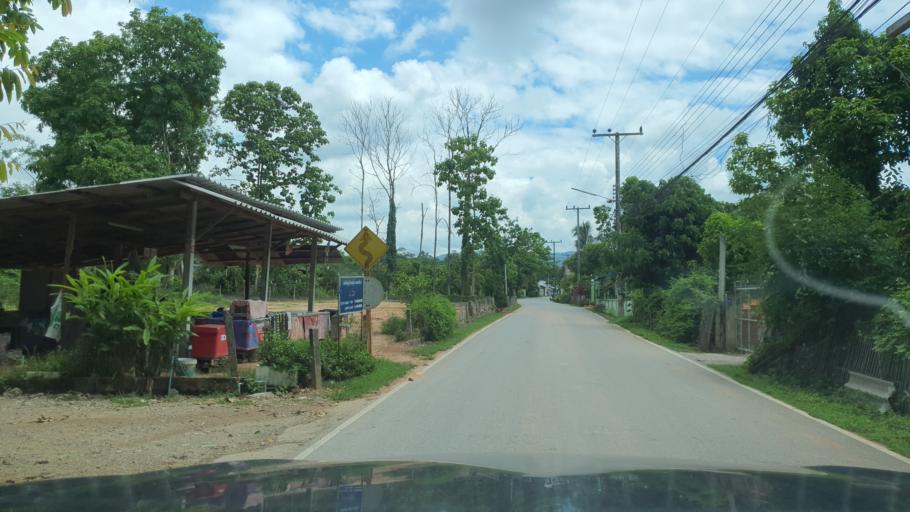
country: TH
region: Chiang Mai
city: San Sai
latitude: 18.9026
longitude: 99.0416
